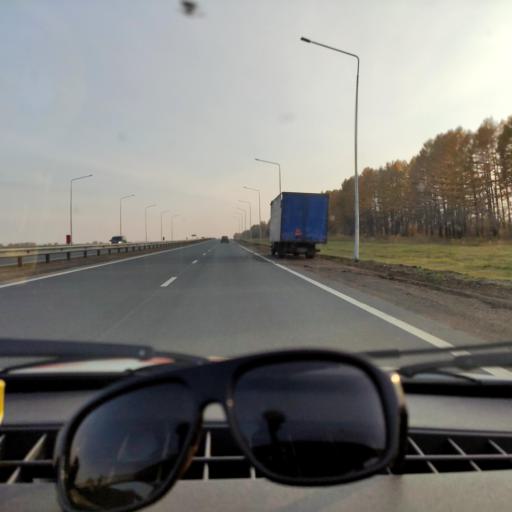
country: RU
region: Bashkortostan
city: Sterlitamak
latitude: 53.7658
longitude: 55.9448
